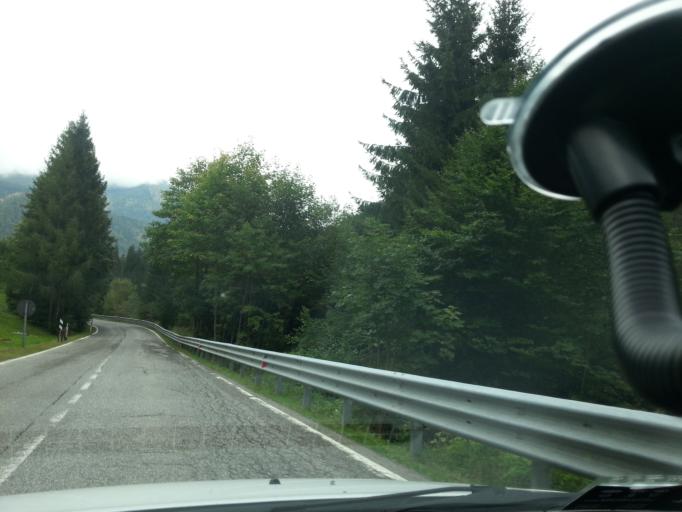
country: IT
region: Friuli Venezia Giulia
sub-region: Provincia di Udine
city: Forni Avoltri
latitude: 46.5776
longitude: 12.7573
